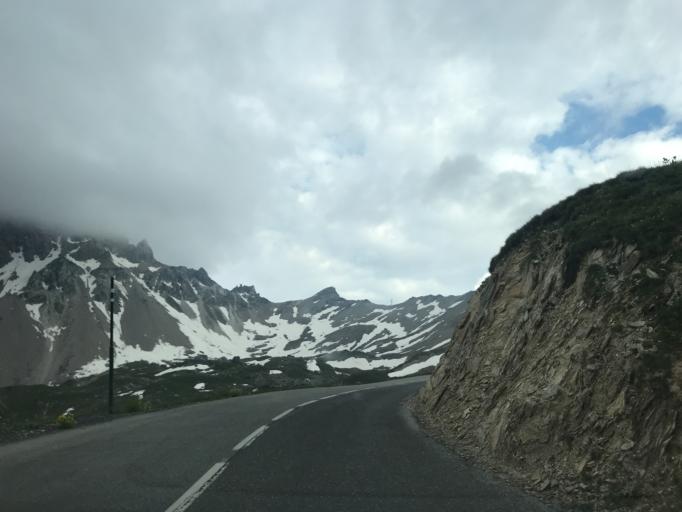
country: FR
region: Rhone-Alpes
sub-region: Departement de la Savoie
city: Valloire
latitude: 45.0756
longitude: 6.4128
